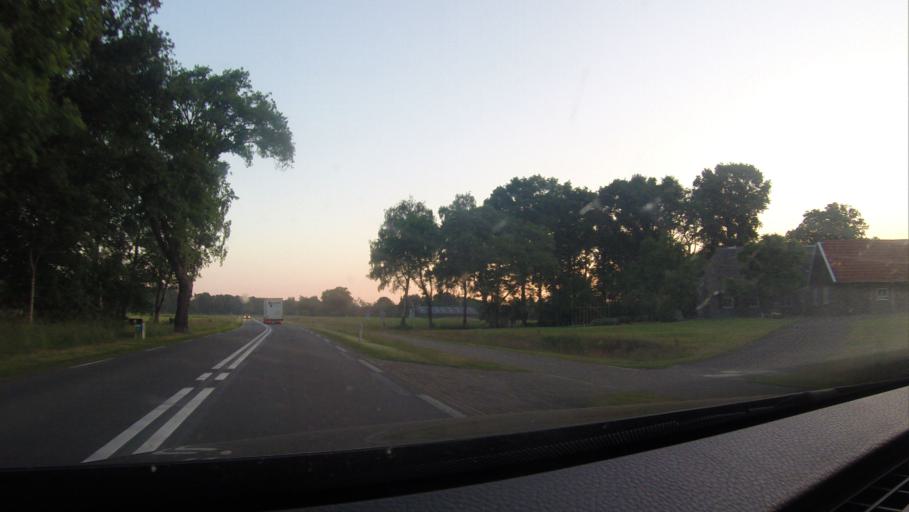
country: NL
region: Overijssel
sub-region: Gemeente Raalte
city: Raalte
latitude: 52.3437
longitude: 6.2766
